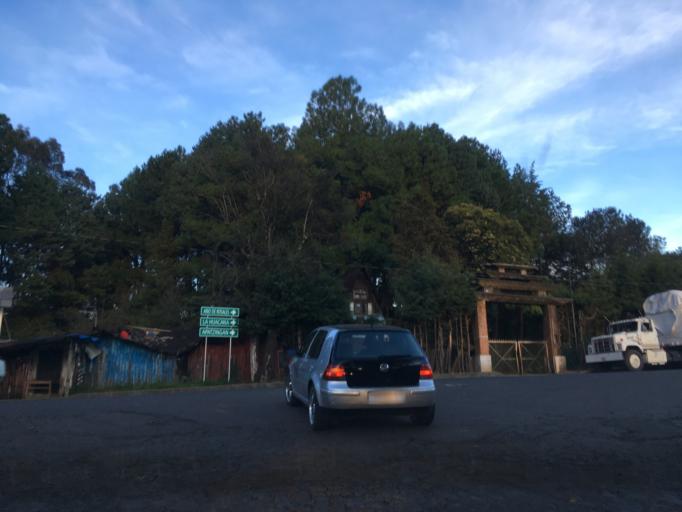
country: MX
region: Michoacan
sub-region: Salvador Escalante
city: Santa Clara del Cobre
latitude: 19.4001
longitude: -101.6503
